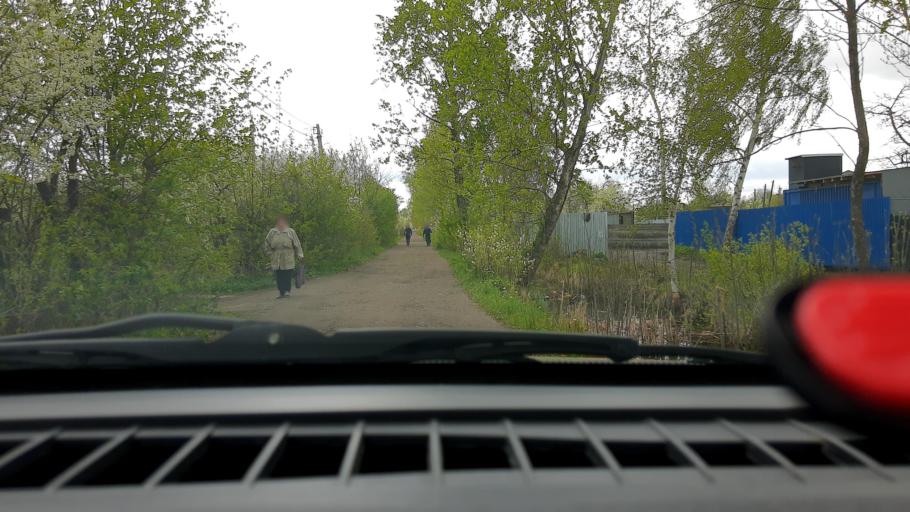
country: RU
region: Nizjnij Novgorod
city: Gorbatovka
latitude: 56.2411
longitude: 43.8134
